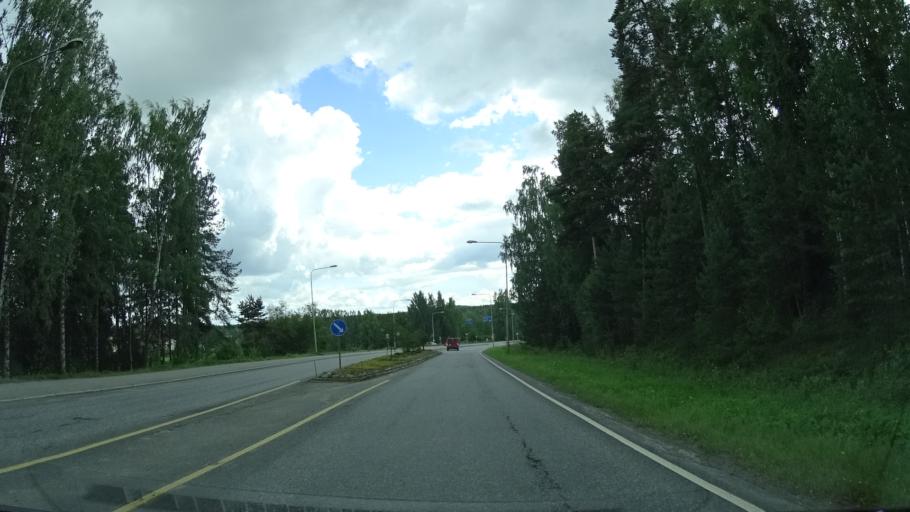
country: FI
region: Pirkanmaa
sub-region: Etelae-Pirkanmaa
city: Valkeakoski
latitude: 61.2542
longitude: 24.0340
